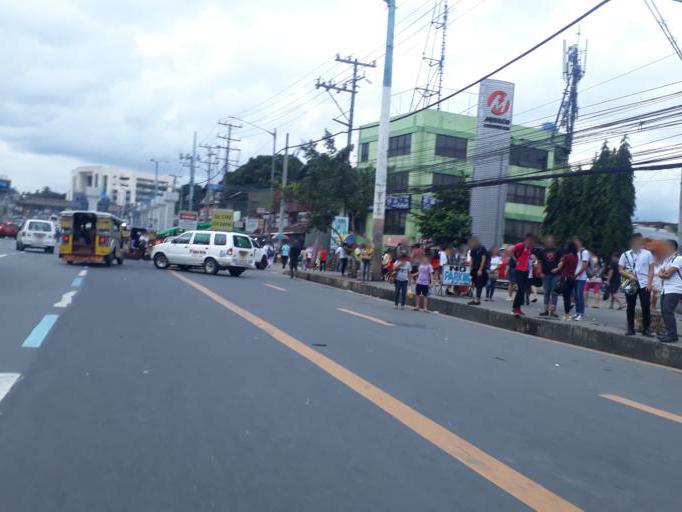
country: PH
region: Calabarzon
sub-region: Province of Rizal
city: San Mateo
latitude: 14.6836
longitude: 121.0860
